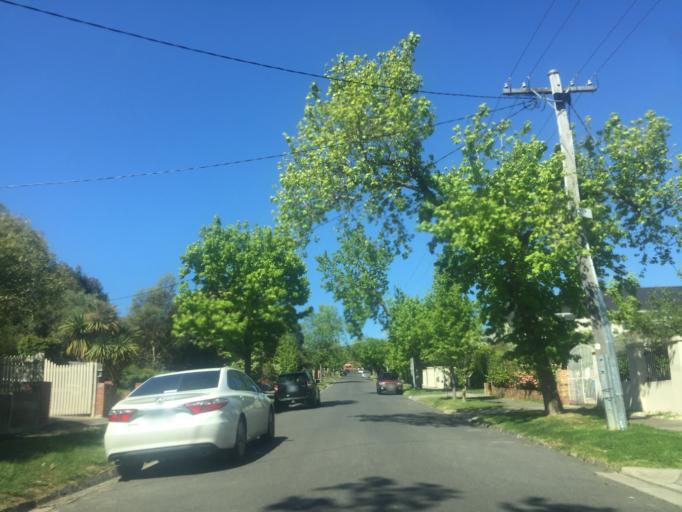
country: AU
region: Victoria
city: Balwyn
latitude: -37.8066
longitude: 145.0792
